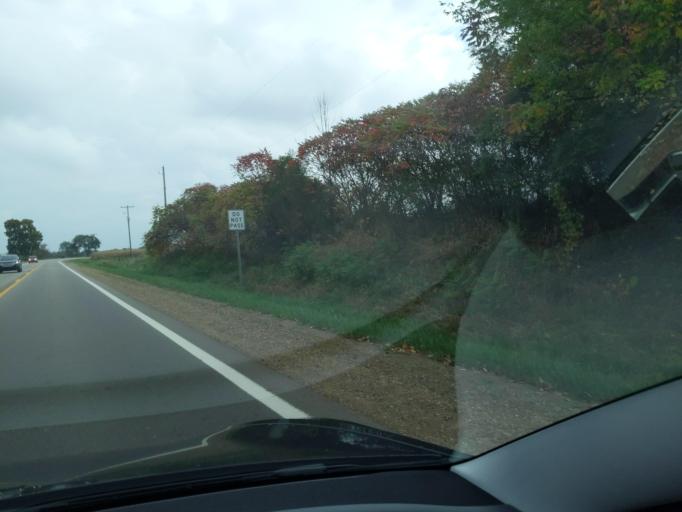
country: US
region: Michigan
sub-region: Eaton County
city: Eaton Rapids
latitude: 42.5309
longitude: -84.7132
